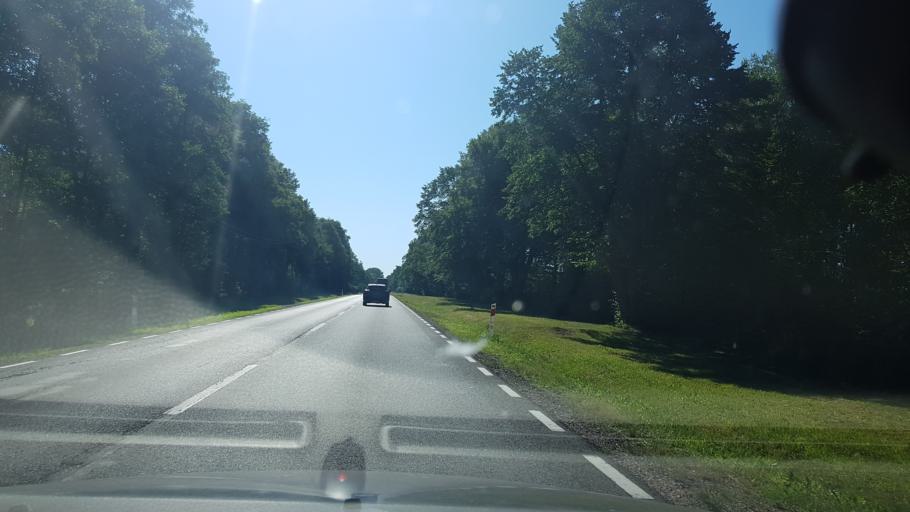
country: PL
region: Masovian Voivodeship
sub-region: Powiat wegrowski
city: Lochow
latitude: 52.5522
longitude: 21.6129
